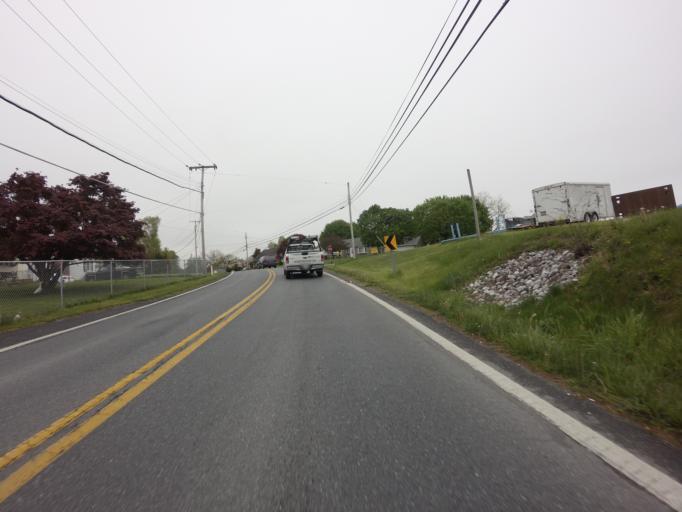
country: US
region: Maryland
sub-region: Carroll County
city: Hampstead
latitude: 39.6110
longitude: -76.8525
